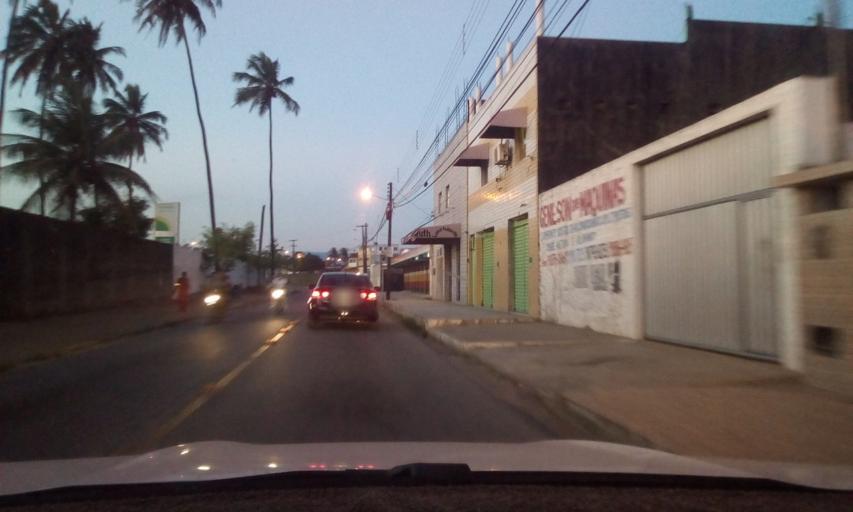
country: BR
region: Paraiba
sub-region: Bayeux
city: Bayeux
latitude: -7.1614
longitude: -34.9060
